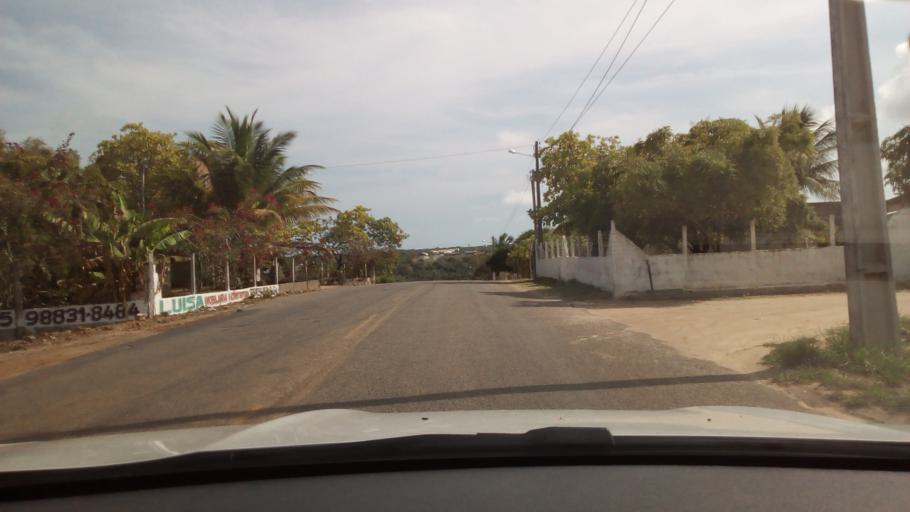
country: BR
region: Paraiba
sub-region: Conde
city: Conde
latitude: -7.3076
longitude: -34.8096
